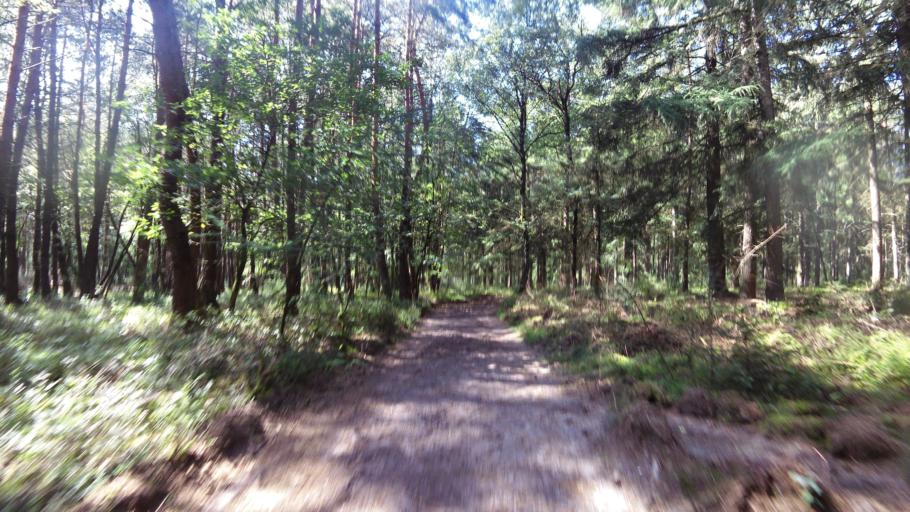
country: NL
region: Gelderland
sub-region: Gemeente Ede
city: Otterlo
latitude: 52.0561
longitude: 5.7503
